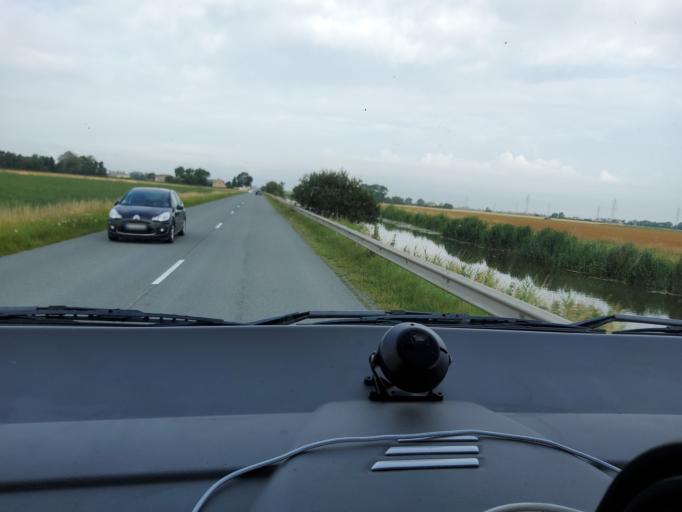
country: FR
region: Nord-Pas-de-Calais
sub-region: Departement du Nord
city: Looberghe
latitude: 50.9526
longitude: 2.2432
